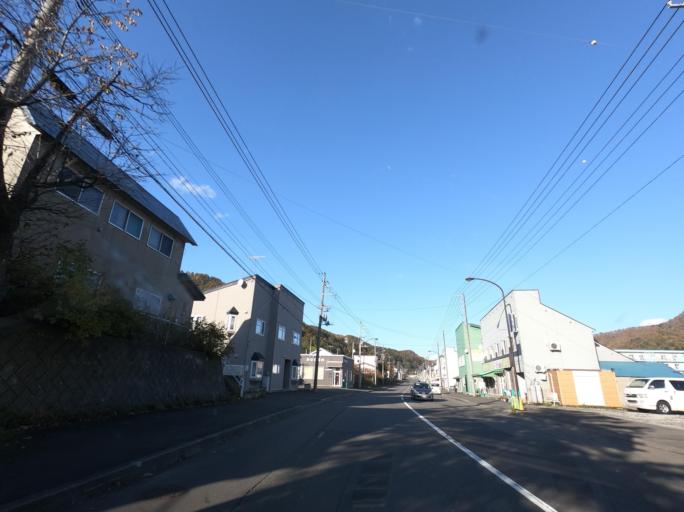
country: JP
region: Hokkaido
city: Iwamizawa
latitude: 43.0464
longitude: 141.9634
